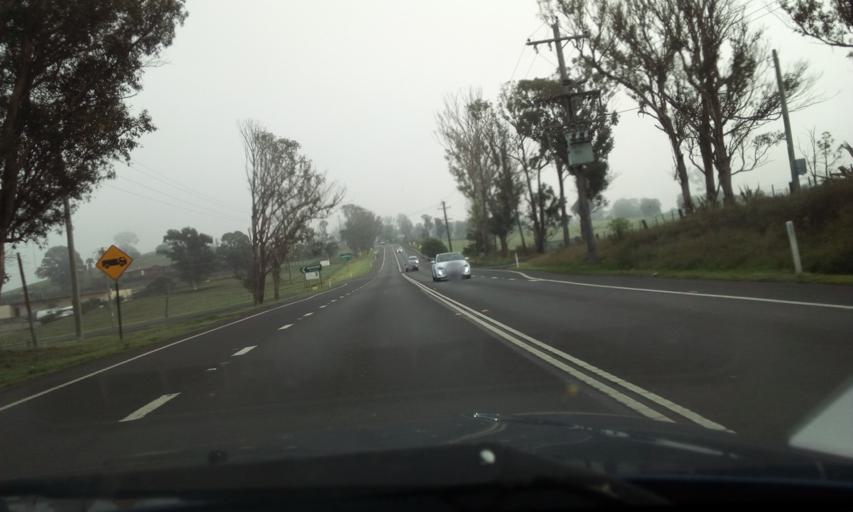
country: AU
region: New South Wales
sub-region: Liverpool
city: Luddenham
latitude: -33.8473
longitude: 150.6882
